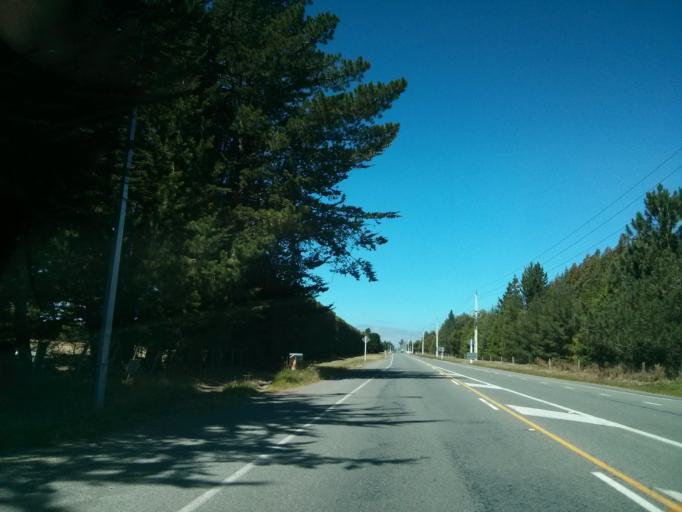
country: NZ
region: Canterbury
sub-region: Waimakariri District
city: Kaiapoi
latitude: -43.3674
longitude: 172.4897
